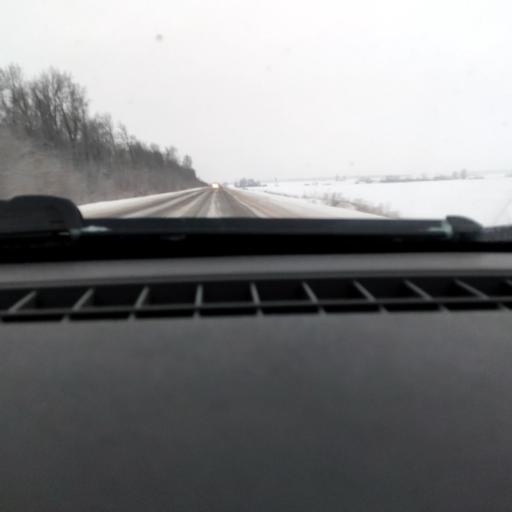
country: RU
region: Bashkortostan
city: Ulukulevo
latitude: 54.3921
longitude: 56.3808
